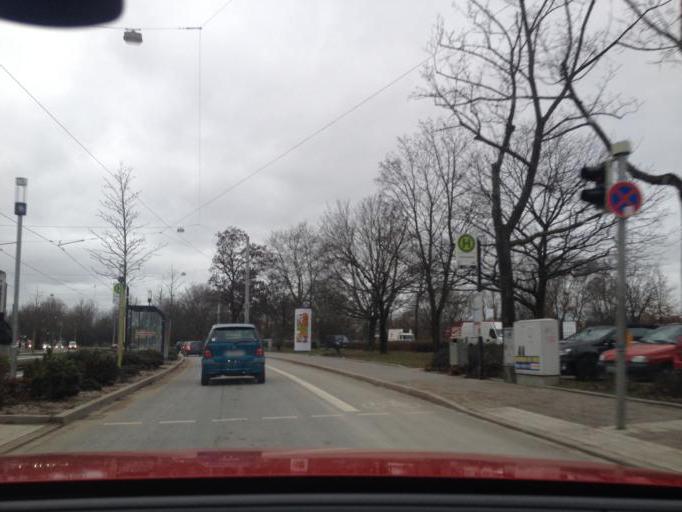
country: DE
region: Bavaria
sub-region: Regierungsbezirk Mittelfranken
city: Nuernberg
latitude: 49.4507
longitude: 11.1036
